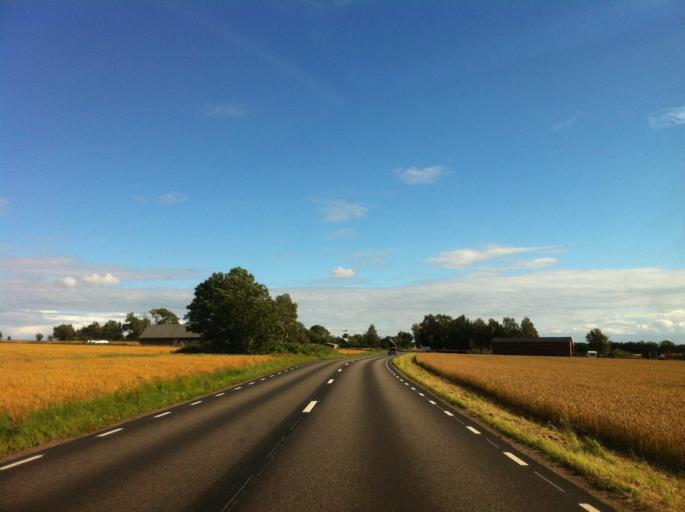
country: SE
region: Skane
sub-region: Angelholms Kommun
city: AEngelholm
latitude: 56.2971
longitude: 12.8738
